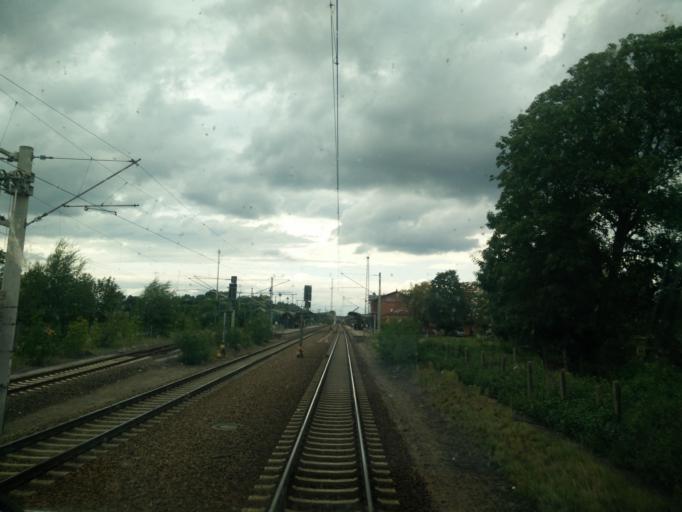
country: DE
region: Brandenburg
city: Luebben
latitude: 51.9386
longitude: 13.8791
